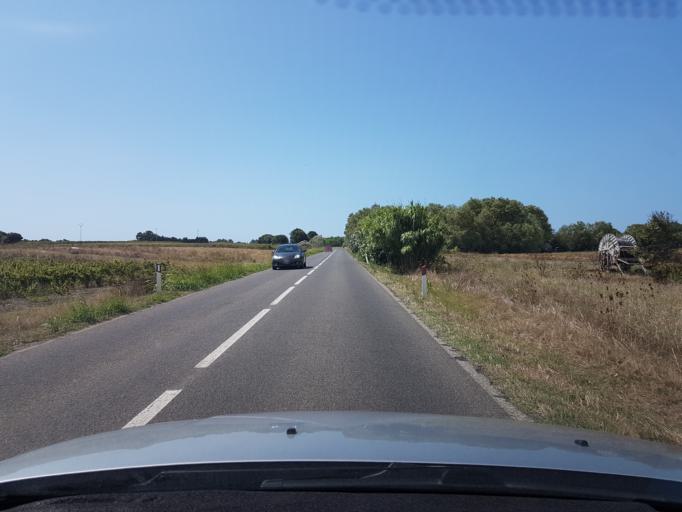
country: IT
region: Sardinia
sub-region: Provincia di Oristano
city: Riola Sardo
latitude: 40.0214
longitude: 8.4812
